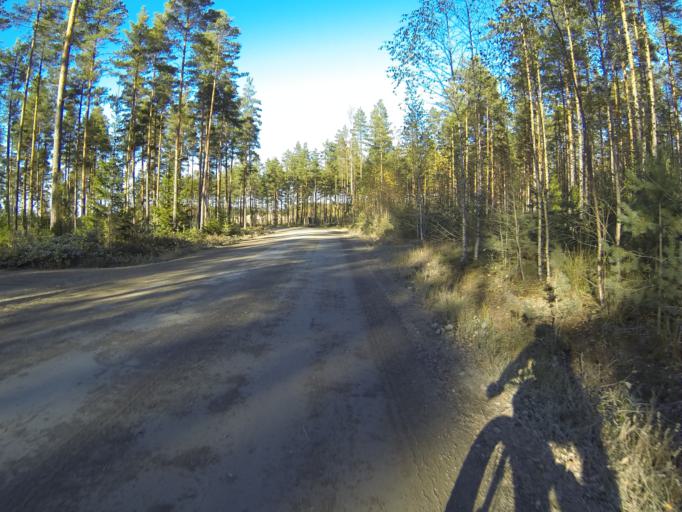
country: FI
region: Varsinais-Suomi
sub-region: Salo
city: Saerkisalo
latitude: 60.2199
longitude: 22.9906
